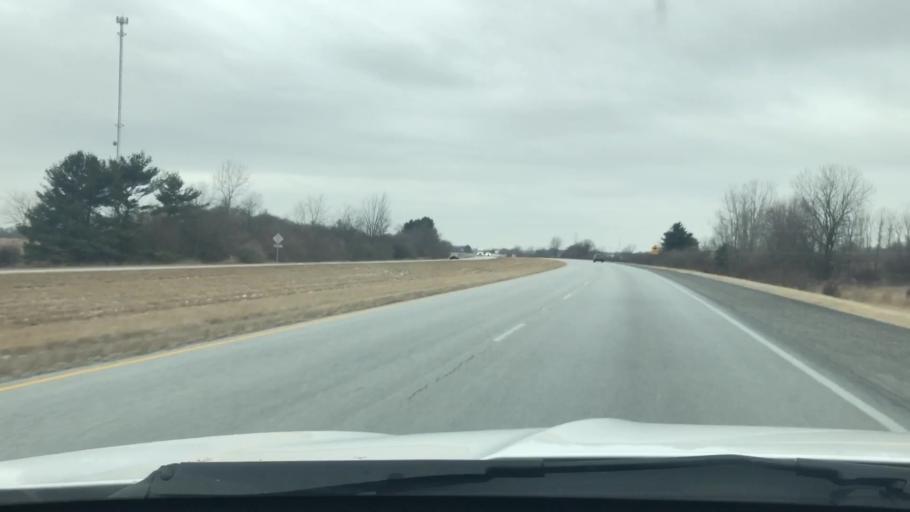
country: US
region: Indiana
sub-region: Miami County
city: Peru
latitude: 40.8836
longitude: -86.1442
